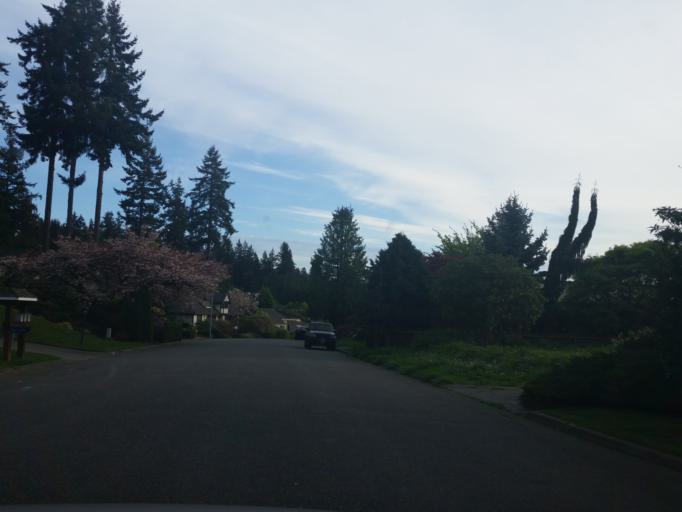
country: US
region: Washington
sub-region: Snohomish County
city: Edmonds
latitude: 47.8145
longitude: -122.3585
